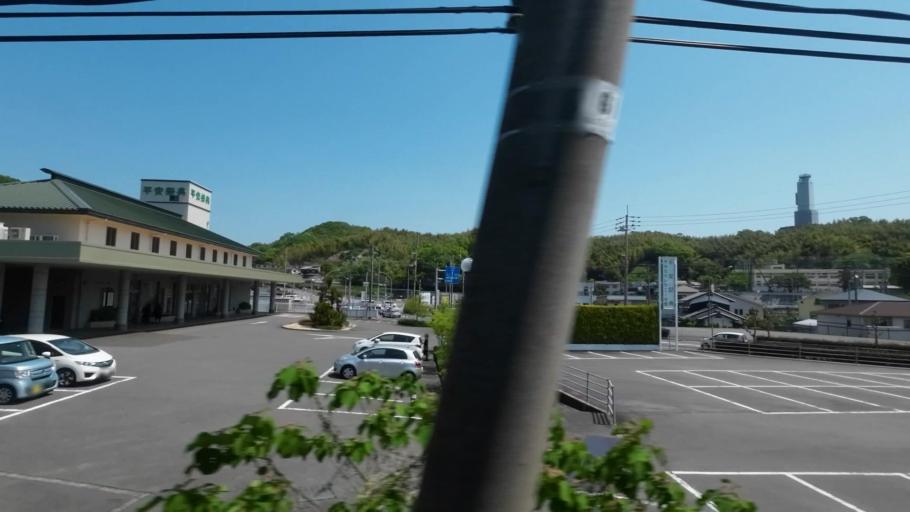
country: JP
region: Ehime
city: Hojo
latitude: 34.0892
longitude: 132.9827
